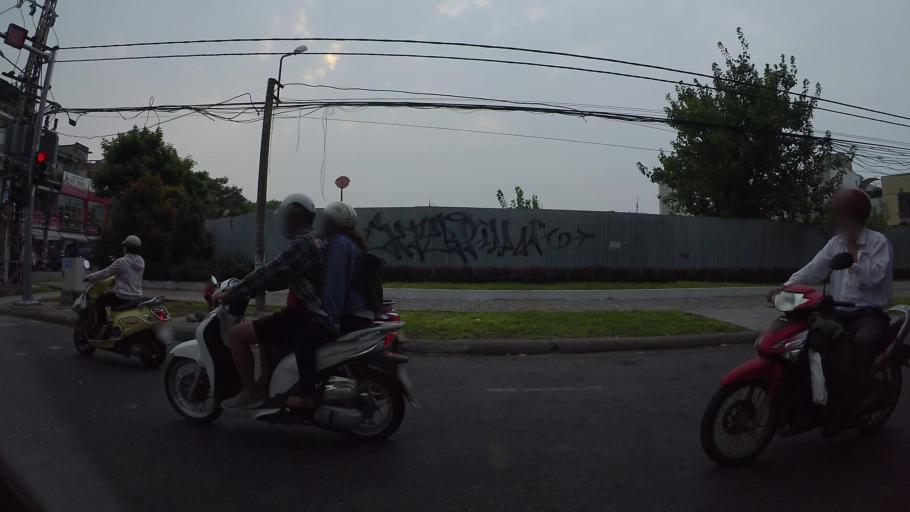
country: VN
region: Da Nang
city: Da Nang
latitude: 16.0688
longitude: 108.2203
